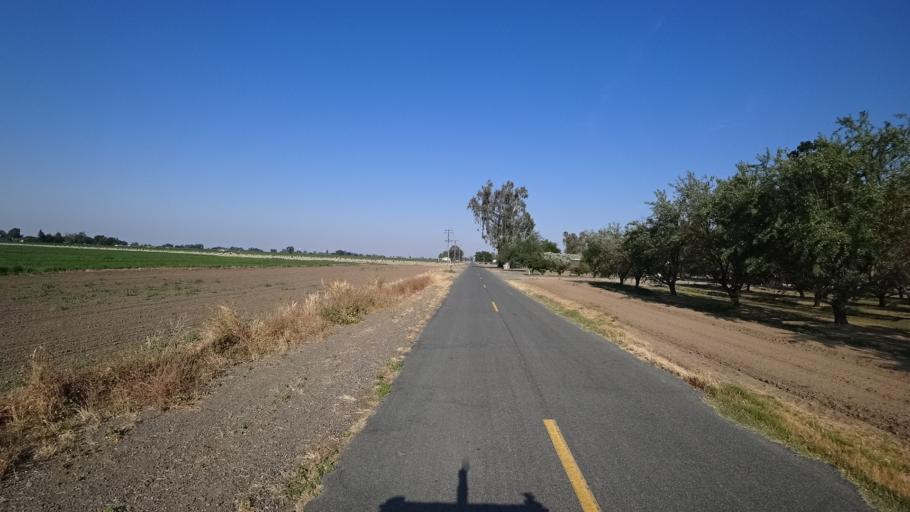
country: US
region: California
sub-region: Fresno County
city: Riverdale
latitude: 36.3585
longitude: -119.8370
